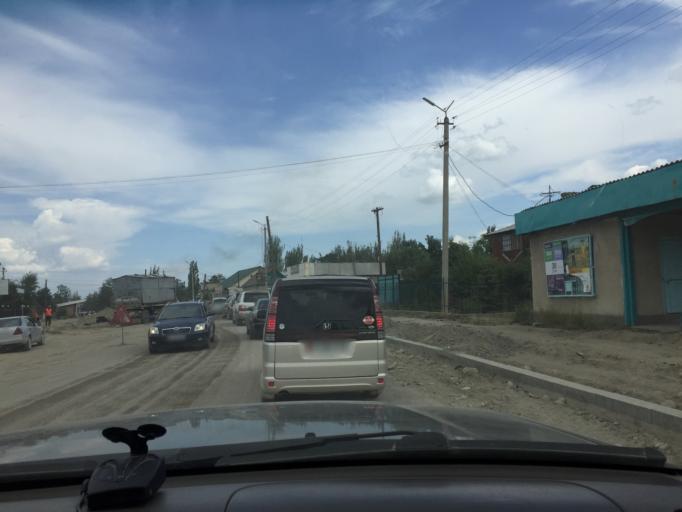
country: KG
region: Ysyk-Koel
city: Karakol
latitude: 42.4843
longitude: 78.3819
